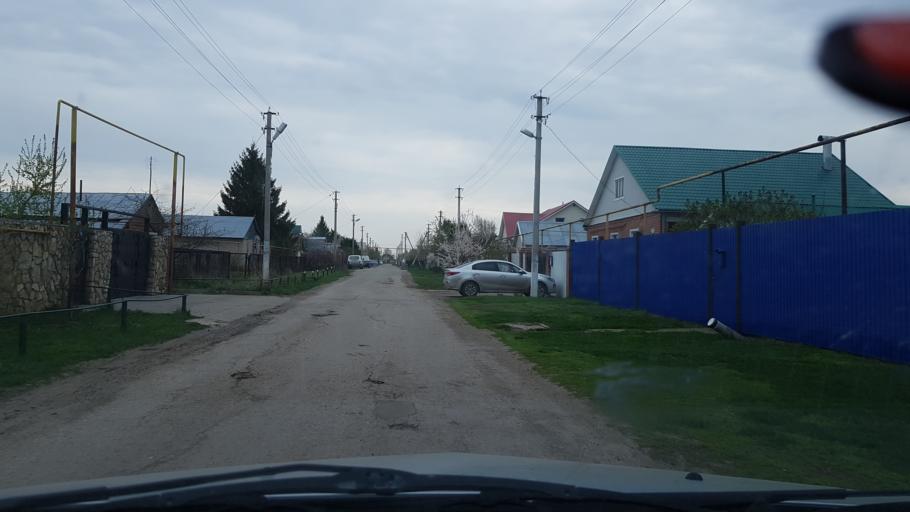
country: RU
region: Samara
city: Khryashchevka
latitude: 53.6711
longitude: 49.0680
